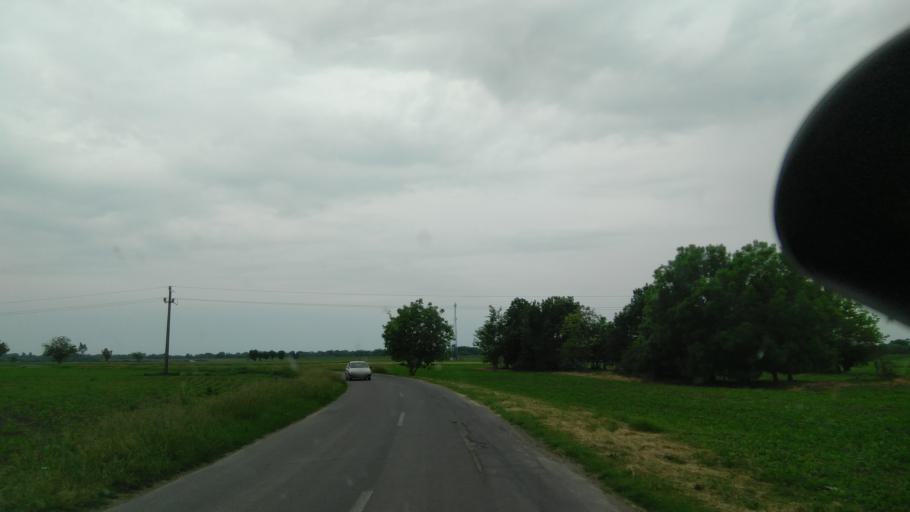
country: HU
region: Bekes
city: Doboz
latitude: 46.7254
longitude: 21.2407
